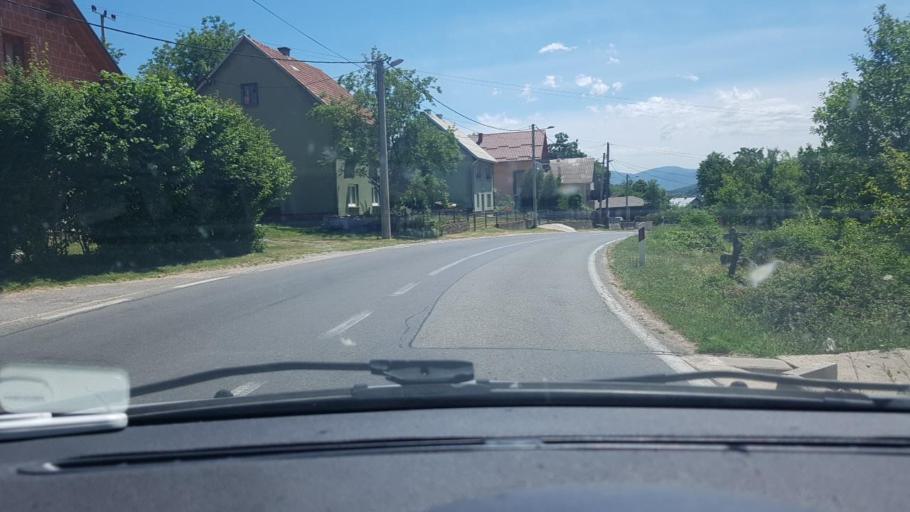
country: HR
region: Licko-Senjska
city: Otocac
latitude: 44.8741
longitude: 15.2121
